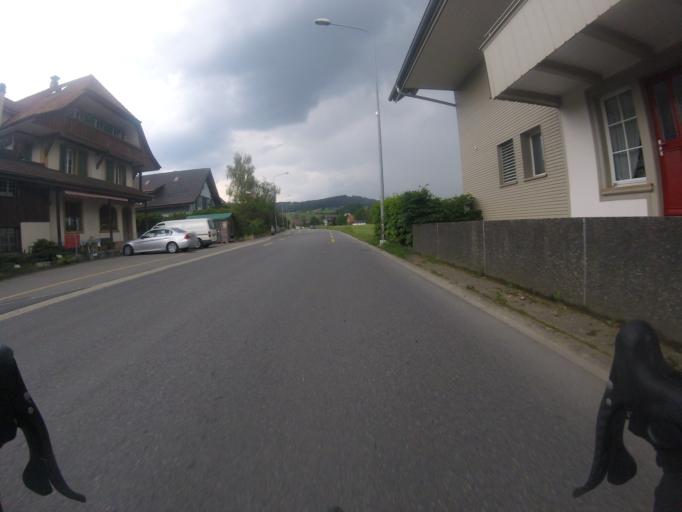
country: CH
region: Bern
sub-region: Bern-Mittelland District
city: Niederwichtrach
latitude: 46.8412
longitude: 7.5700
